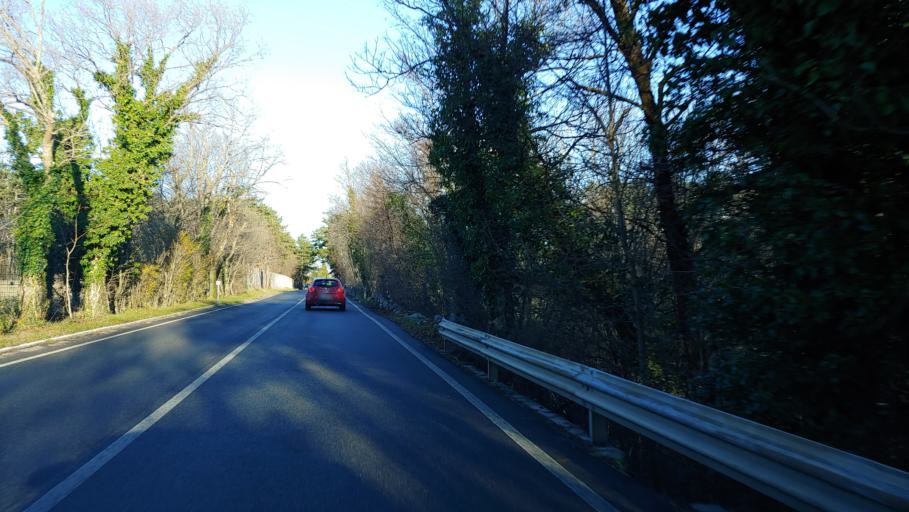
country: IT
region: Friuli Venezia Giulia
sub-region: Provincia di Trieste
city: Trieste
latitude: 45.6642
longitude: 13.8331
